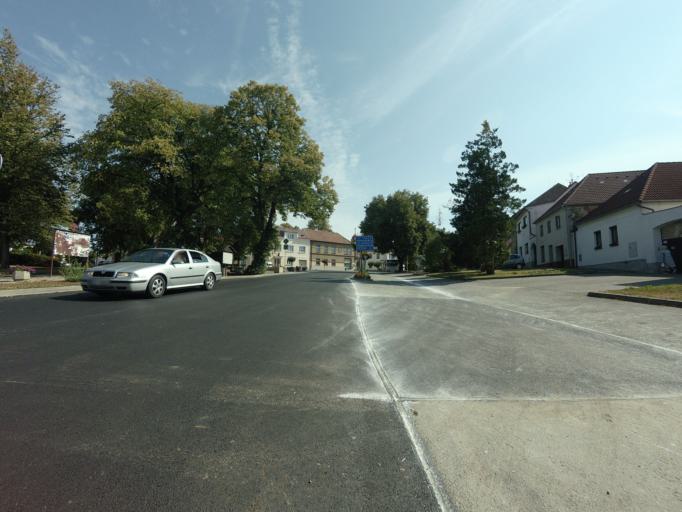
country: CZ
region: Jihocesky
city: Bernartice
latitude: 49.3684
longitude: 14.3800
